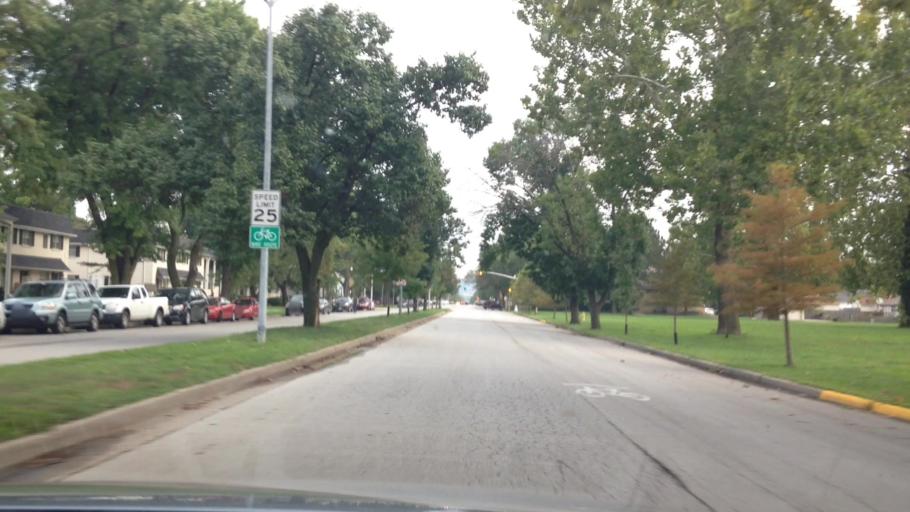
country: US
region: Missouri
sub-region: Clay County
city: North Kansas City
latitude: 39.1466
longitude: -94.5772
